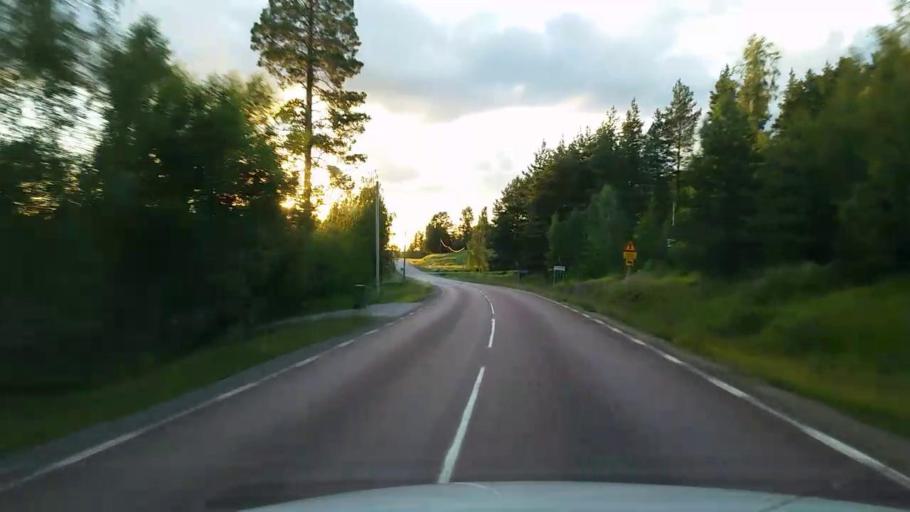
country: SE
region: Vaesternorrland
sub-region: Ange Kommun
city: Ange
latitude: 62.1519
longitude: 15.6816
